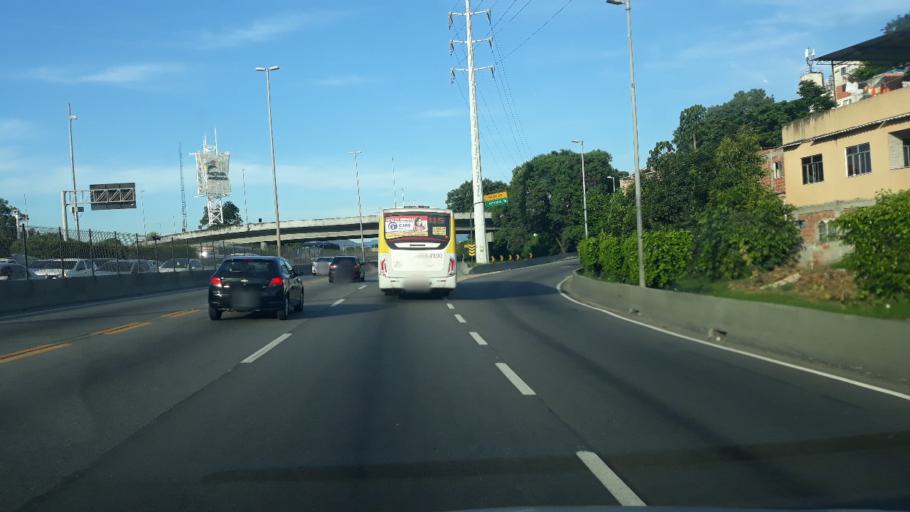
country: BR
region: Rio de Janeiro
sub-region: Rio De Janeiro
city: Rio de Janeiro
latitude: -22.8754
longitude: -43.2722
